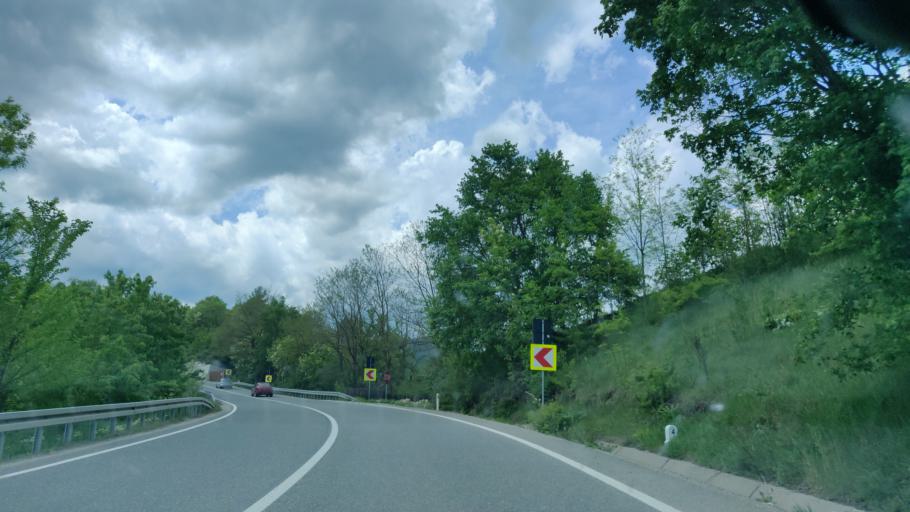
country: RO
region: Vrancea
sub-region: Comuna Negrilesti
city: Negrilesti
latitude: 45.9225
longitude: 26.6981
